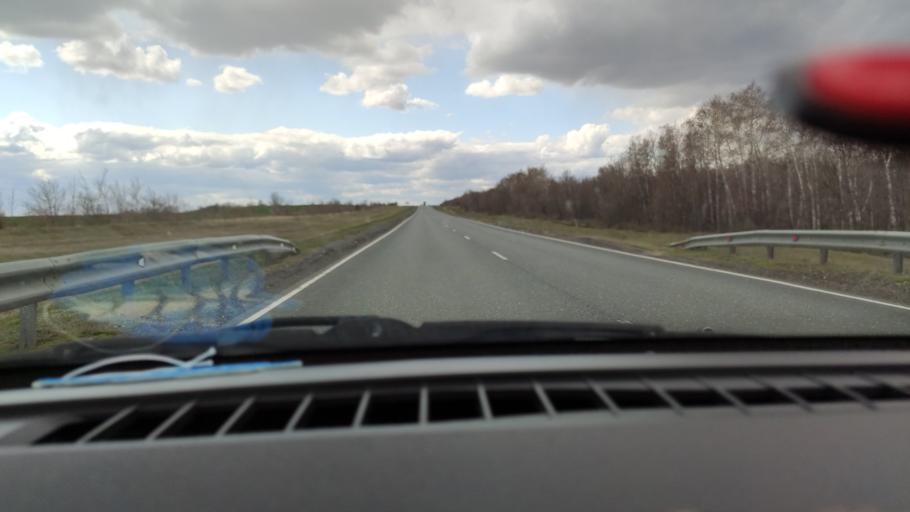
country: RU
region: Saratov
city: Balakovo
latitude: 52.1825
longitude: 47.8436
